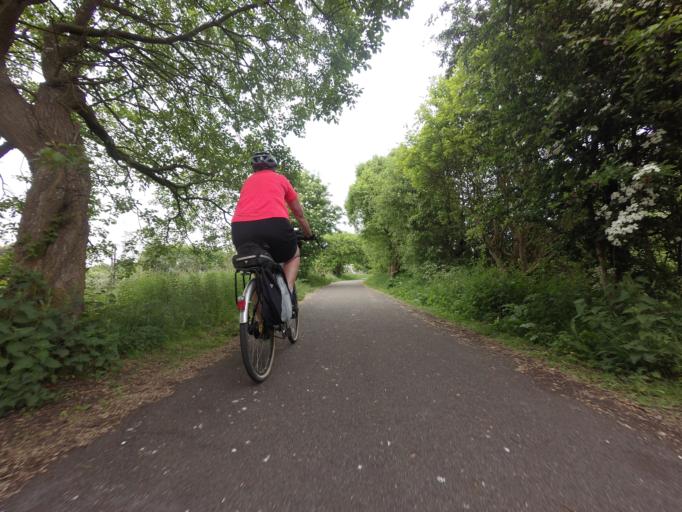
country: GB
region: Scotland
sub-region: Fife
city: Townhill
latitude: 56.0907
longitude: -3.4455
